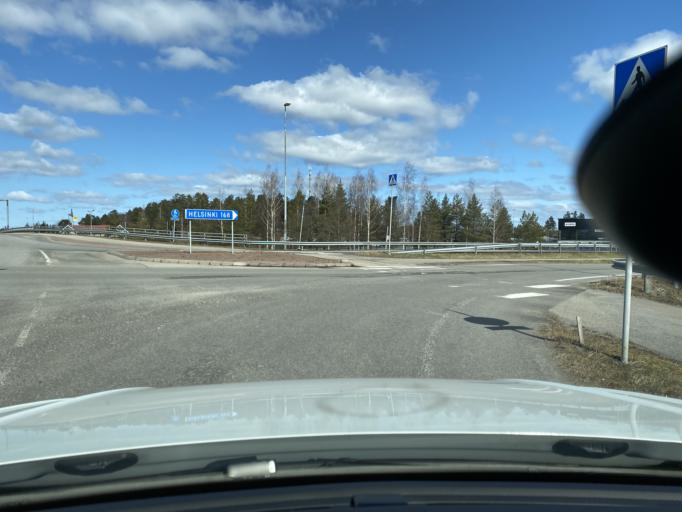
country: FI
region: Varsinais-Suomi
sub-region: Turku
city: Rusko
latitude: 60.4954
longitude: 22.2316
